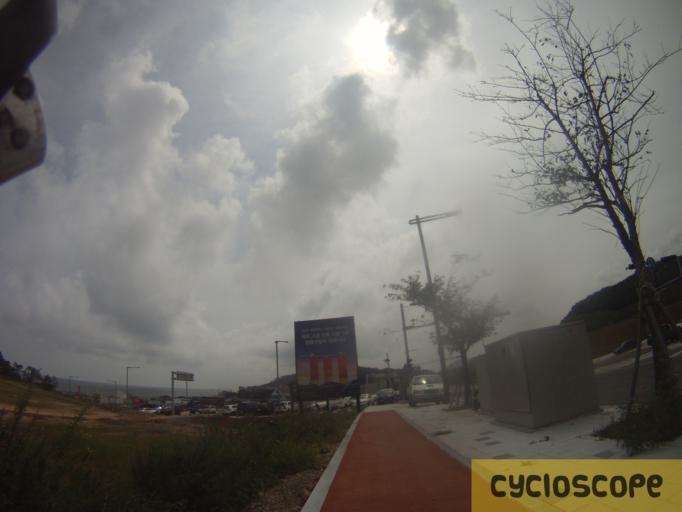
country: KR
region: Busan
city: Kijang
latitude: 35.1969
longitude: 129.2225
